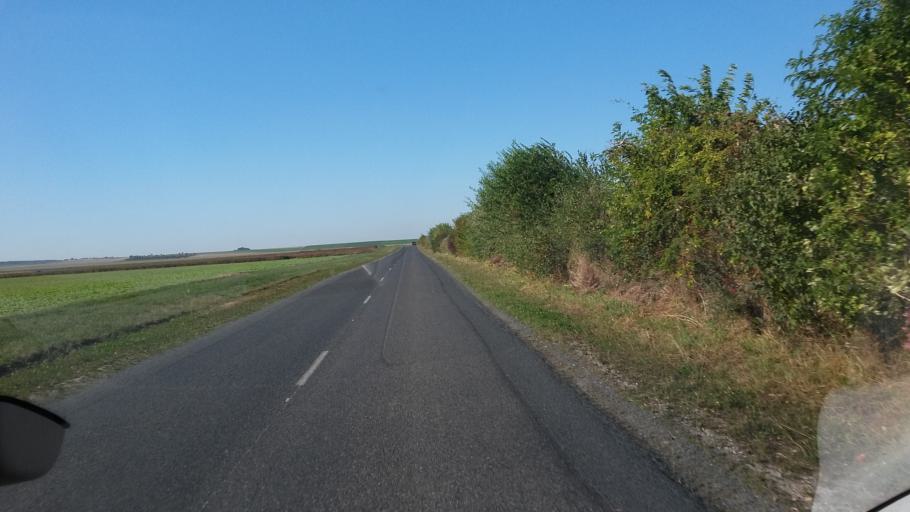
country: FR
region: Champagne-Ardenne
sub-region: Departement de la Marne
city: Connantre
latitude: 48.7426
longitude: 3.8940
